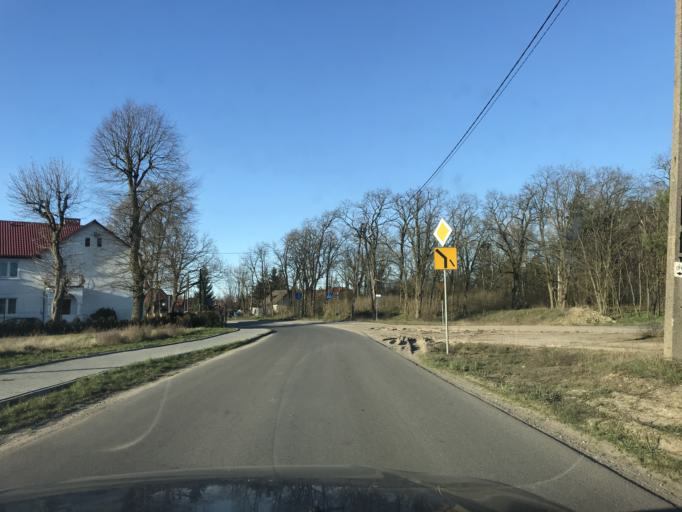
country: PL
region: Lubusz
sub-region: Powiat gorzowski
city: Deszczno
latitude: 52.6492
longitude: 15.3161
